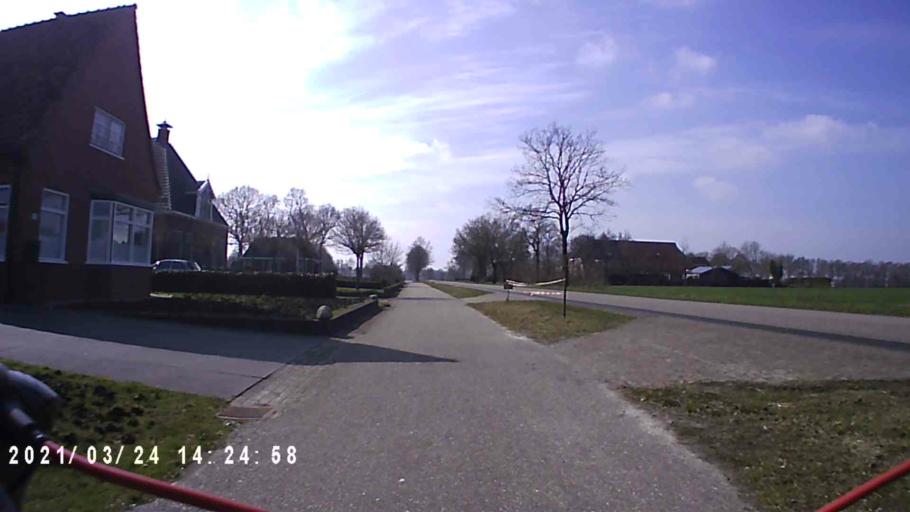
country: NL
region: Friesland
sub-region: Gemeente Heerenveen
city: Jubbega
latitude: 53.0444
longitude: 6.1797
